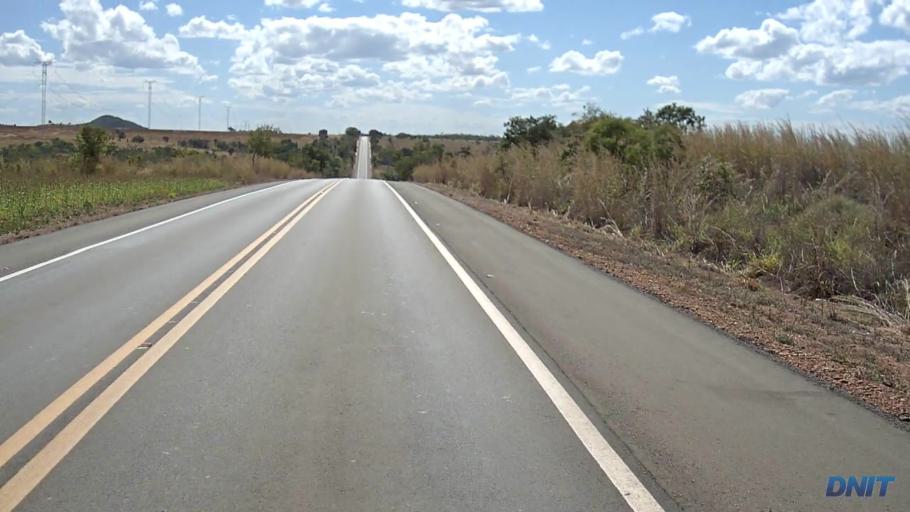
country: BR
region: Goias
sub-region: Barro Alto
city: Barro Alto
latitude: -14.8131
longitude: -49.0428
